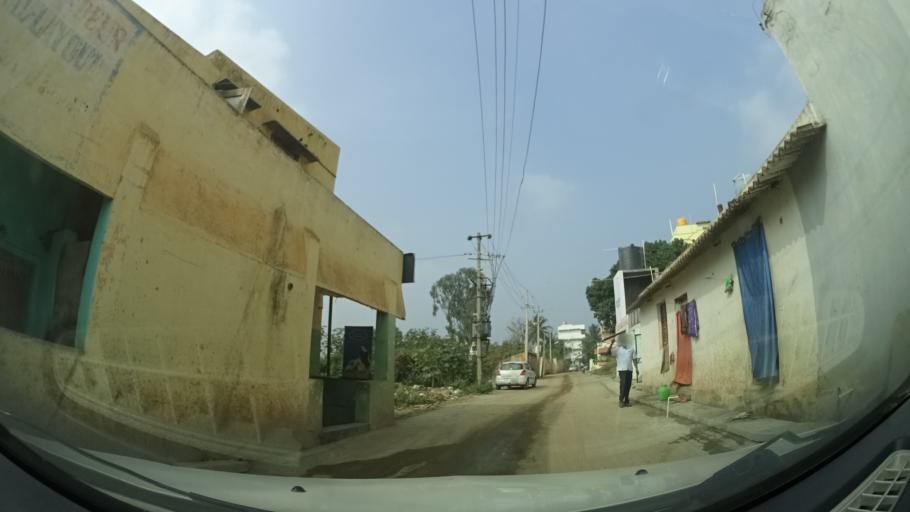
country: IN
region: Karnataka
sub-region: Bangalore Urban
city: Anekal
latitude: 12.7931
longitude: 77.6512
